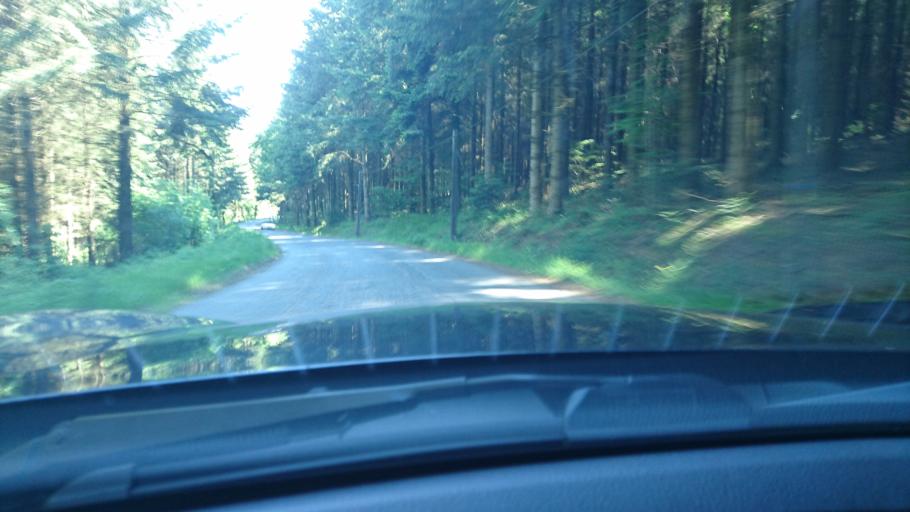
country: FR
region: Rhone-Alpes
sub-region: Departement de la Loire
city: Violay
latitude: 45.8239
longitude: 4.3848
